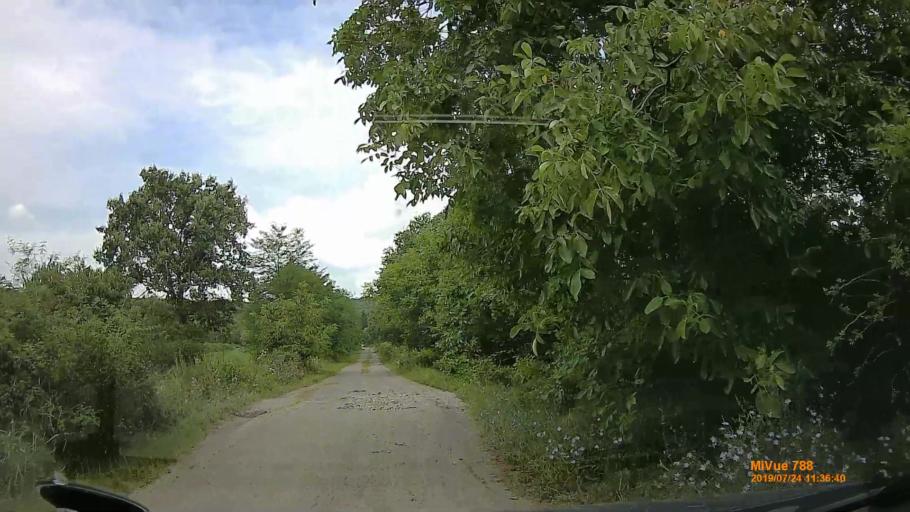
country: UA
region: Zakarpattia
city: Batiovo
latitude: 48.2398
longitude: 22.4769
